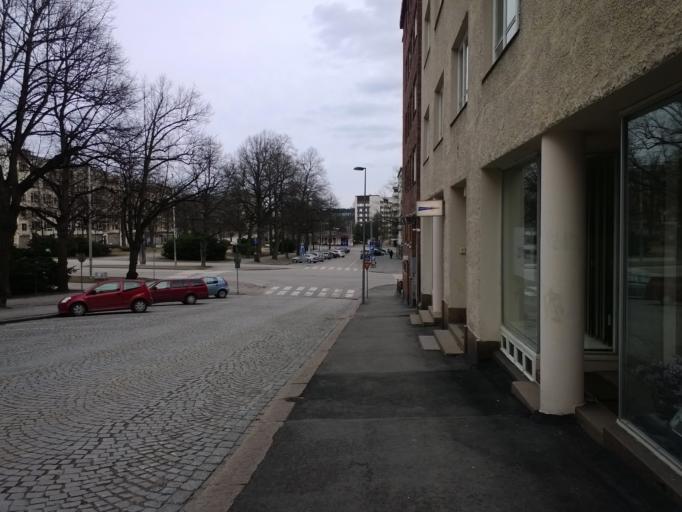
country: FI
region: Paijanne Tavastia
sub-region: Lahti
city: Lahti
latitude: 60.9799
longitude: 25.6565
